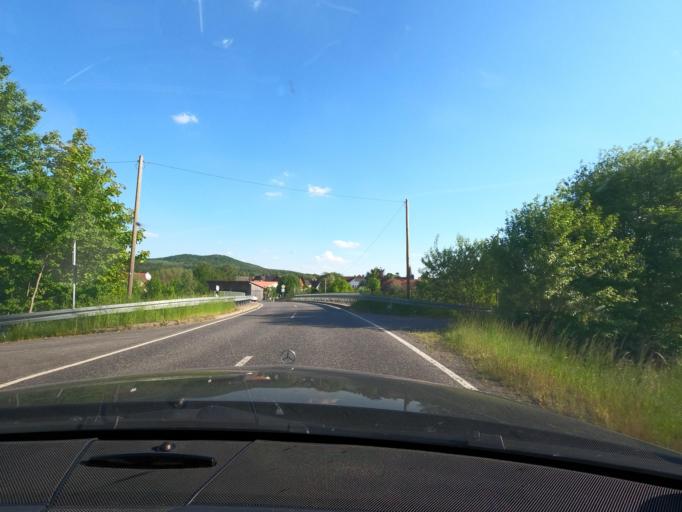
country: DE
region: Hesse
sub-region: Regierungsbezirk Kassel
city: Martinhagen
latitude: 51.3161
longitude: 9.2616
